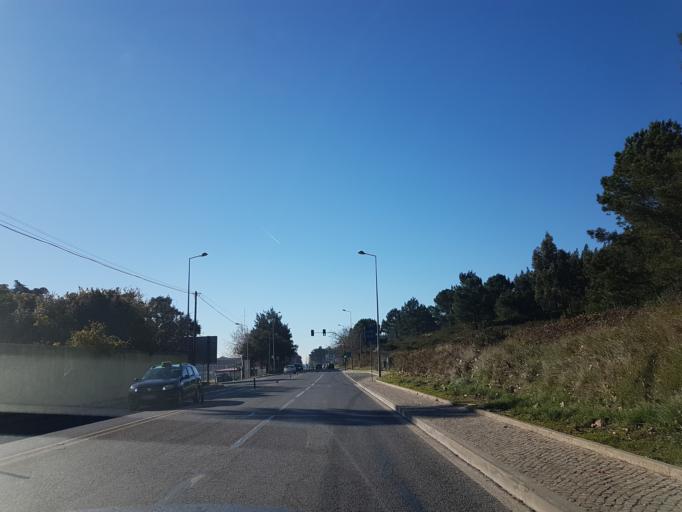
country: PT
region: Lisbon
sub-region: Sintra
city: Sintra
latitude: 38.7855
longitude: -9.3744
